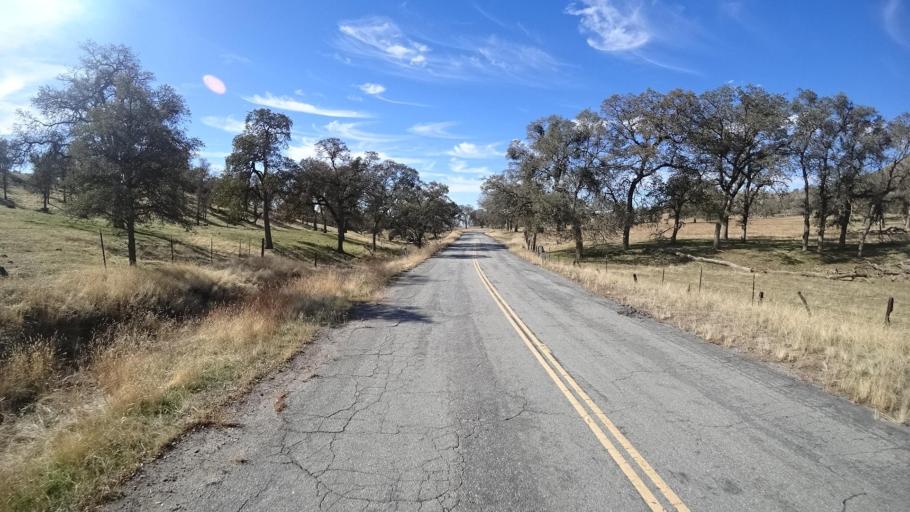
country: US
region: California
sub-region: Kern County
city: Alta Sierra
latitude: 35.6302
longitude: -118.7824
